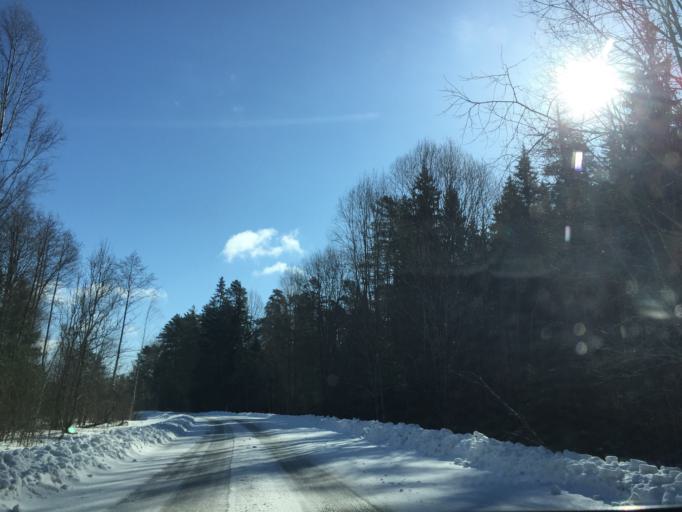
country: LV
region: Aloja
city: Staicele
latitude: 57.9966
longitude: 24.5712
